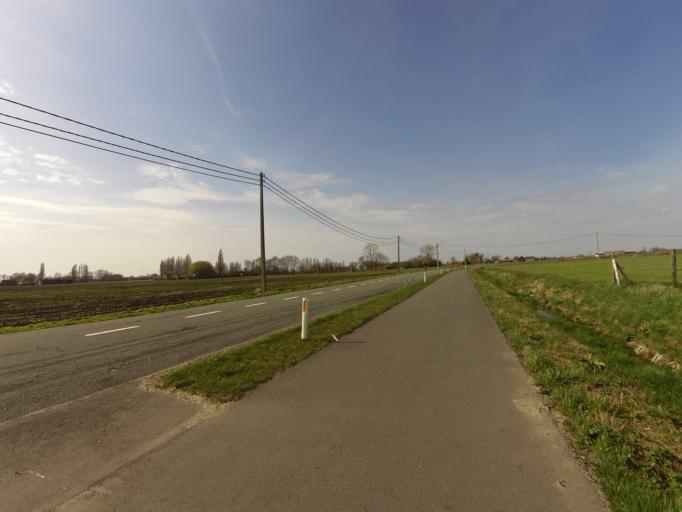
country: BE
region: Flanders
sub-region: Provincie West-Vlaanderen
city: Koekelare
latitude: 51.1065
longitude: 2.9709
